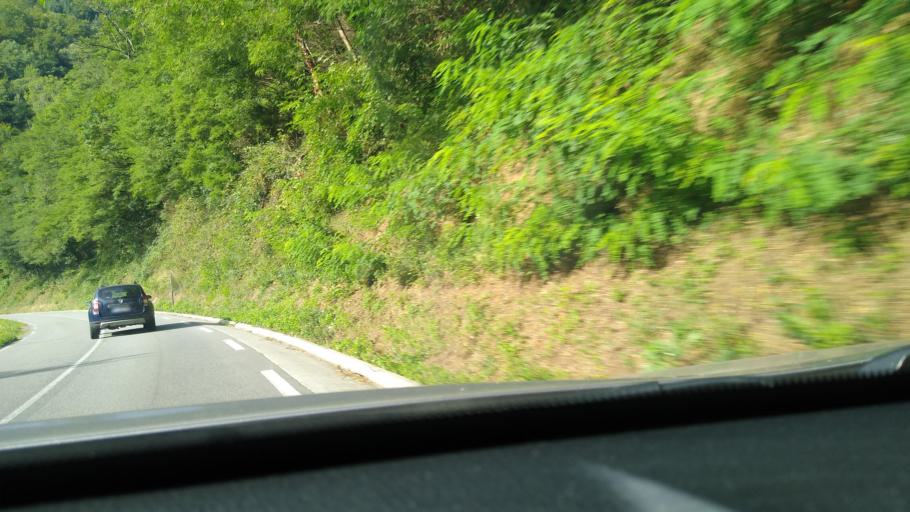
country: FR
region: Midi-Pyrenees
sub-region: Departement de l'Ariege
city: Saint-Girons
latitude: 42.9161
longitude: 1.1915
